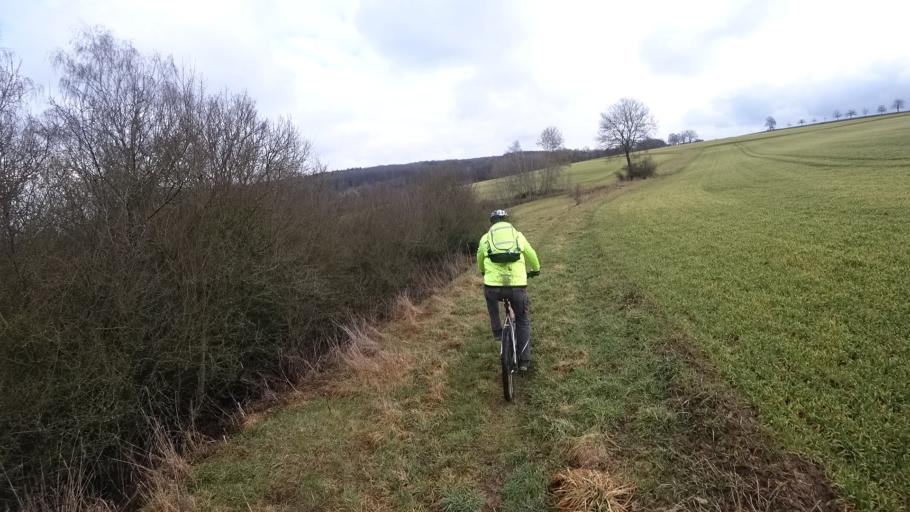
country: DE
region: Rheinland-Pfalz
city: Diethardt
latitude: 50.1769
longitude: 7.8744
